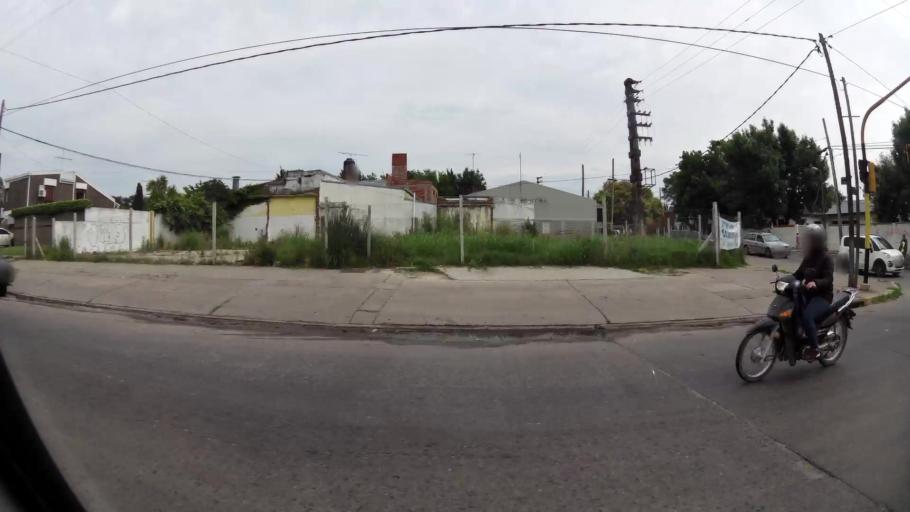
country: AR
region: Buenos Aires
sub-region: Partido de La Plata
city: La Plata
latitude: -34.9209
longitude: -58.0161
